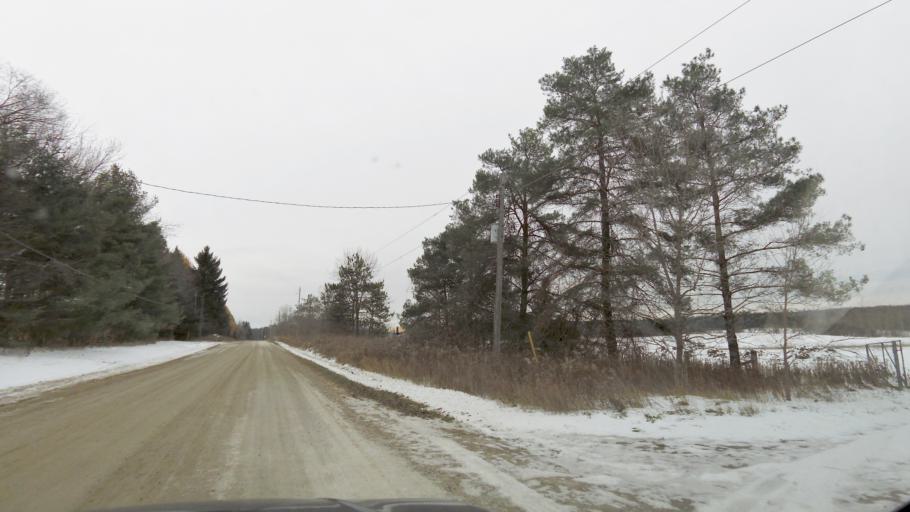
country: CA
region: Ontario
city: Vaughan
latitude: 43.9415
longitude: -79.6104
